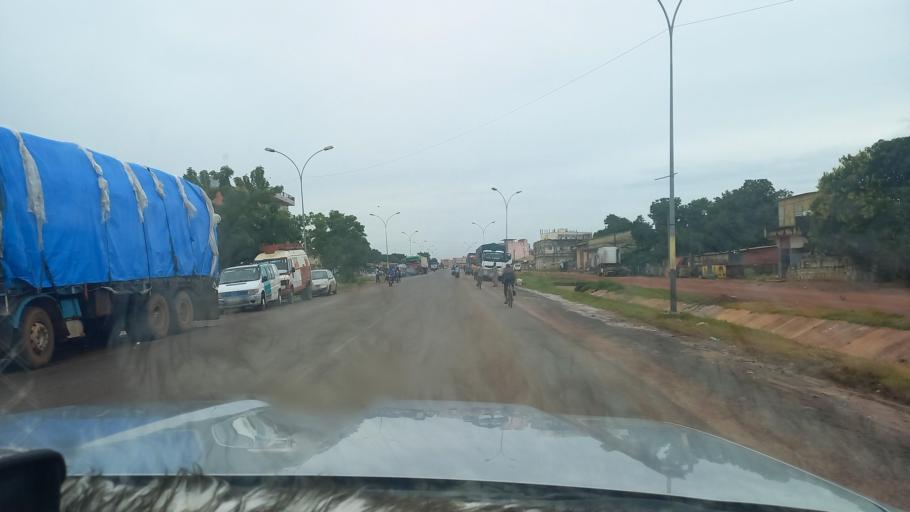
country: SN
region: Ziguinchor
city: Ziguinchor
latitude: 12.5510
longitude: -16.2665
